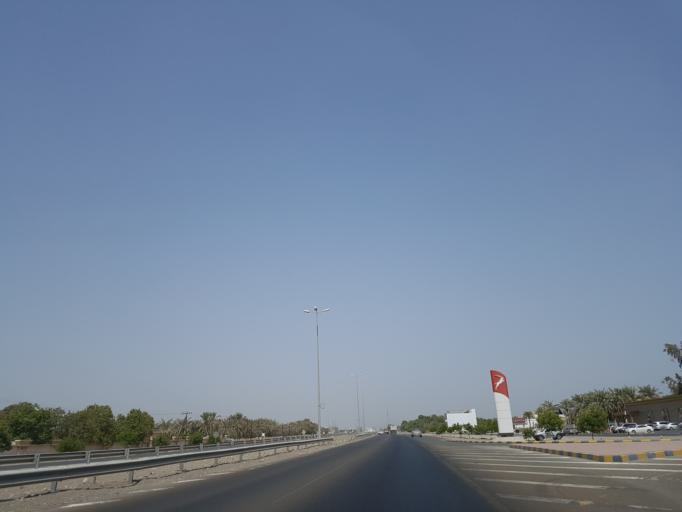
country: OM
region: Al Batinah
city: Saham
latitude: 24.1302
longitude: 56.8940
